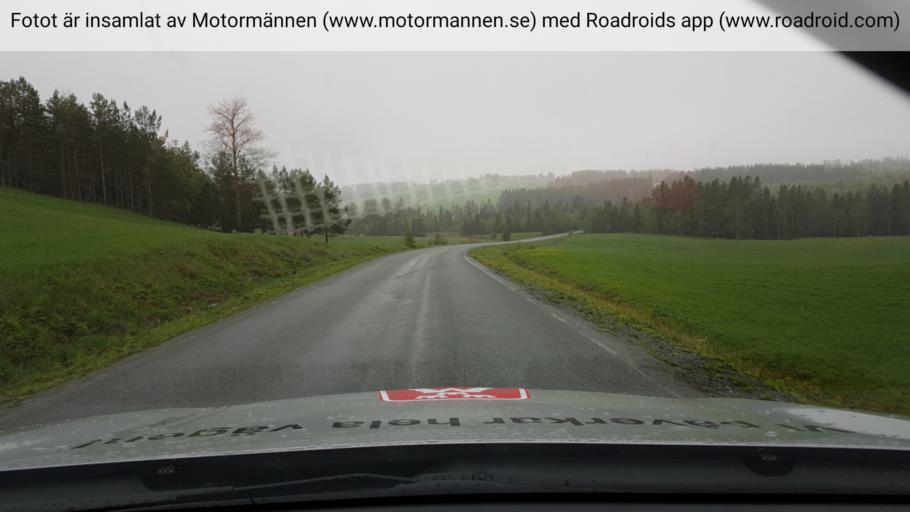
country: SE
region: Jaemtland
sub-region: Bergs Kommun
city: Hoverberg
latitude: 62.9879
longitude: 14.3265
